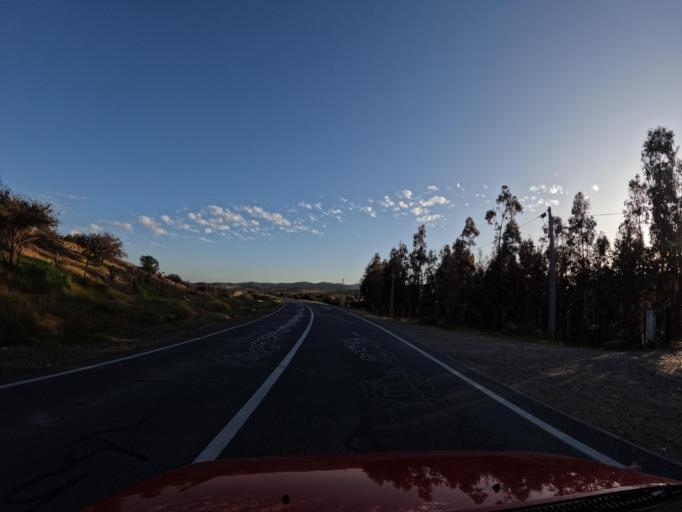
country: CL
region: O'Higgins
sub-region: Provincia de Colchagua
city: Santa Cruz
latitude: -34.3157
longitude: -71.7431
